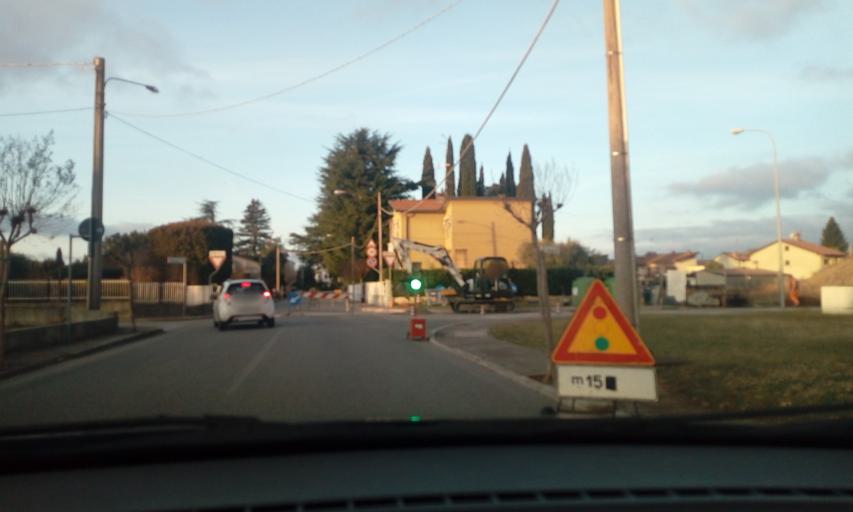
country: IT
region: Friuli Venezia Giulia
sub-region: Provincia di Gorizia
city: Mariano del Friuli
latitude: 45.9140
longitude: 13.4612
